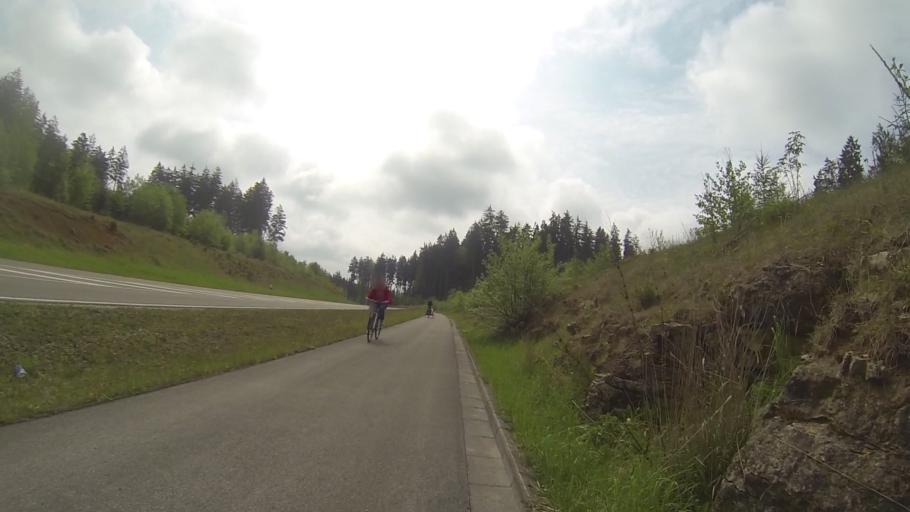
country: DE
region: Baden-Wuerttemberg
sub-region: Regierungsbezirk Stuttgart
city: Nattheim
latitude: 48.6667
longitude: 10.2558
